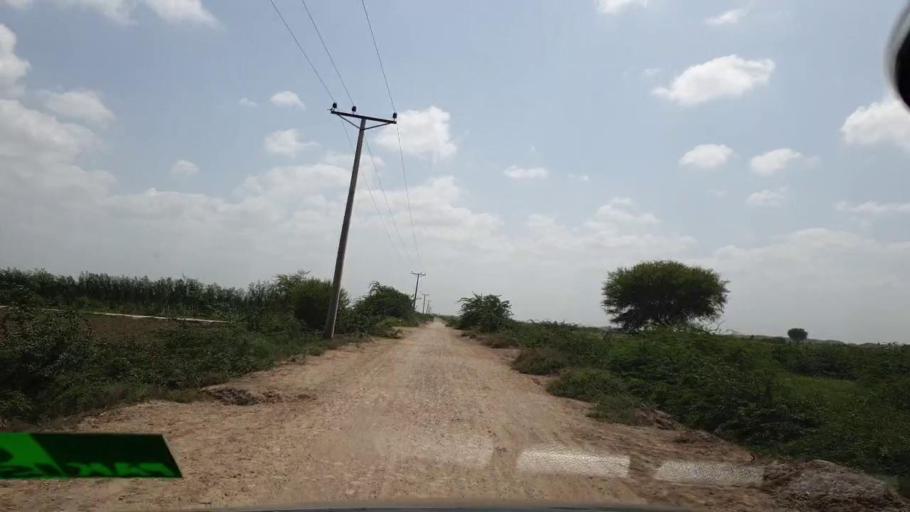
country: PK
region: Sindh
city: Kadhan
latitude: 24.6108
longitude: 69.1853
